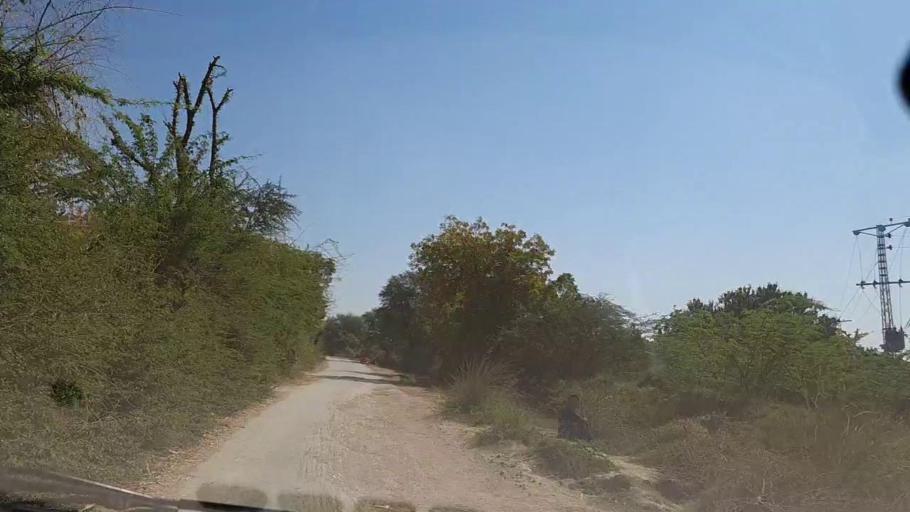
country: PK
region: Sindh
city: Mirpur Khas
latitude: 25.4312
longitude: 69.0204
